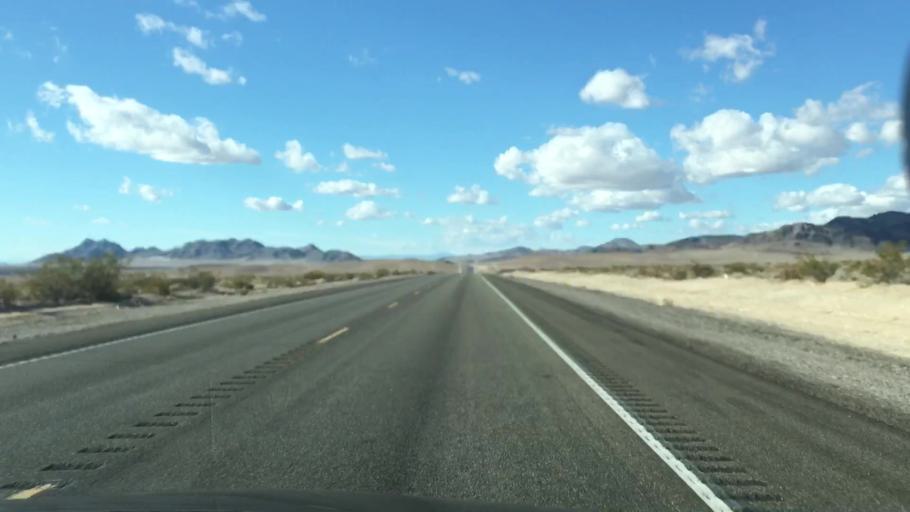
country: US
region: Nevada
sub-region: Nye County
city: Pahrump
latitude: 36.6017
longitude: -116.2507
